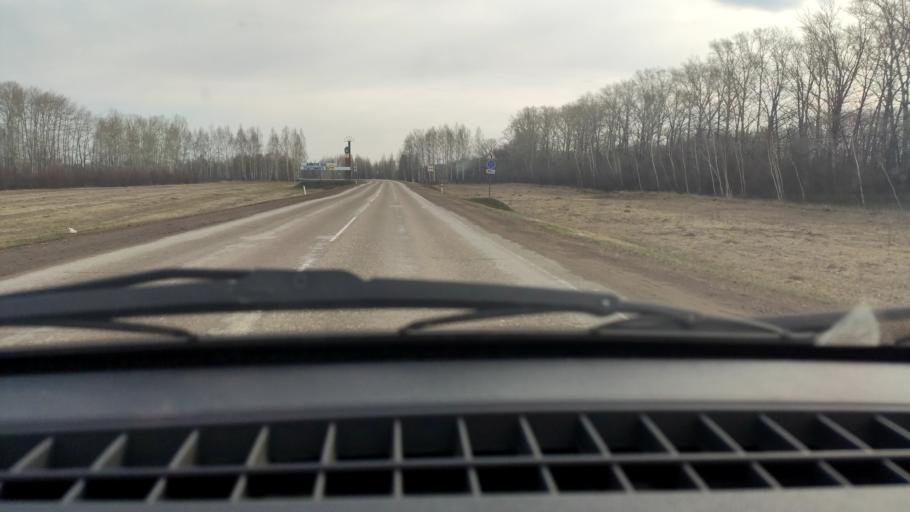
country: RU
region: Bashkortostan
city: Davlekanovo
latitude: 54.3598
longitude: 55.1922
